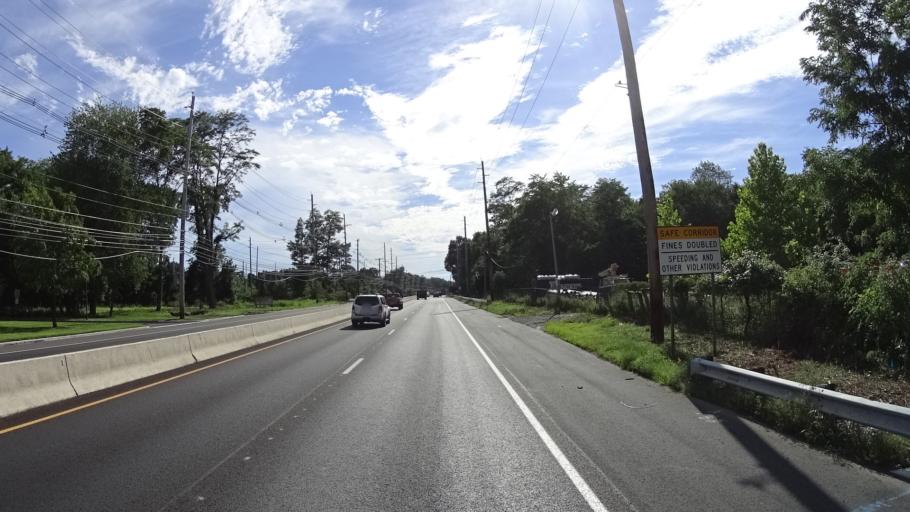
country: US
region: New Jersey
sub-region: Somerset County
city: Bound Brook
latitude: 40.5824
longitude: -74.5168
